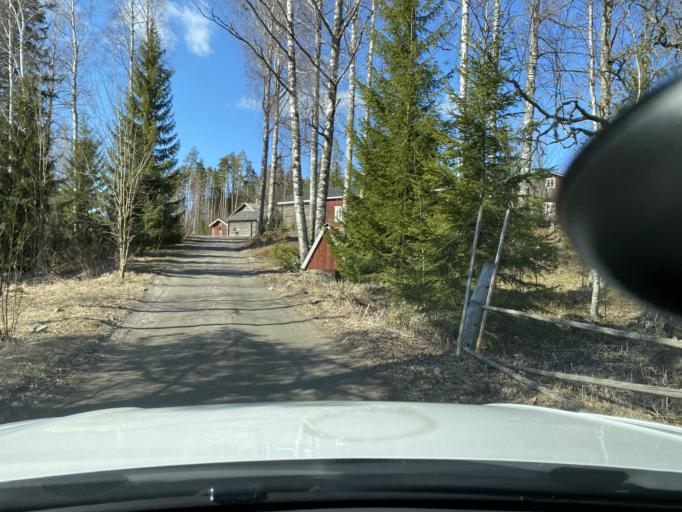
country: FI
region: Pirkanmaa
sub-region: Lounais-Pirkanmaa
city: Punkalaidun
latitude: 61.1087
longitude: 23.1356
